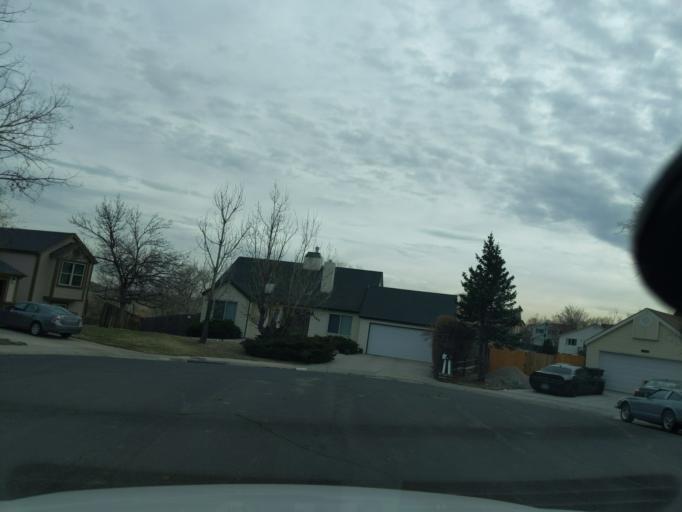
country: US
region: Colorado
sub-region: Adams County
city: Thornton
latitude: 39.8697
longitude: -104.9513
